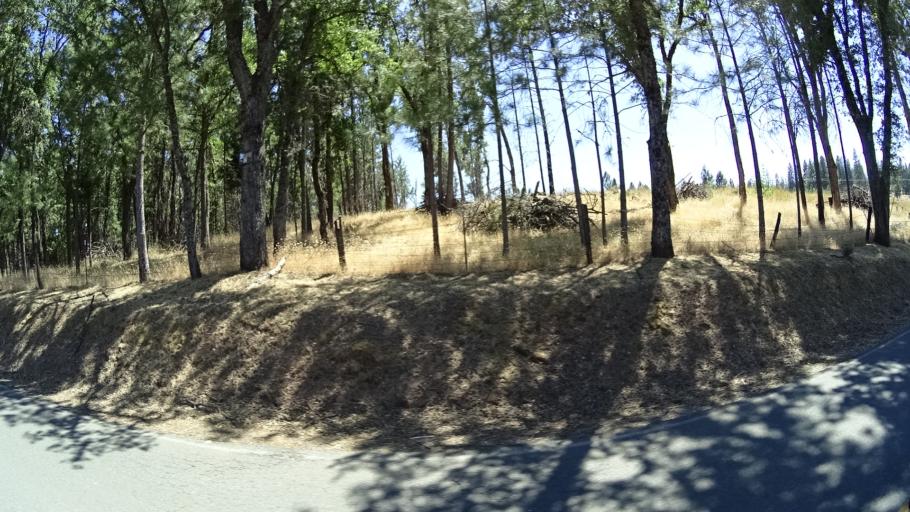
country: US
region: California
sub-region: Calaveras County
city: Mountain Ranch
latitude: 38.2841
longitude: -120.5153
